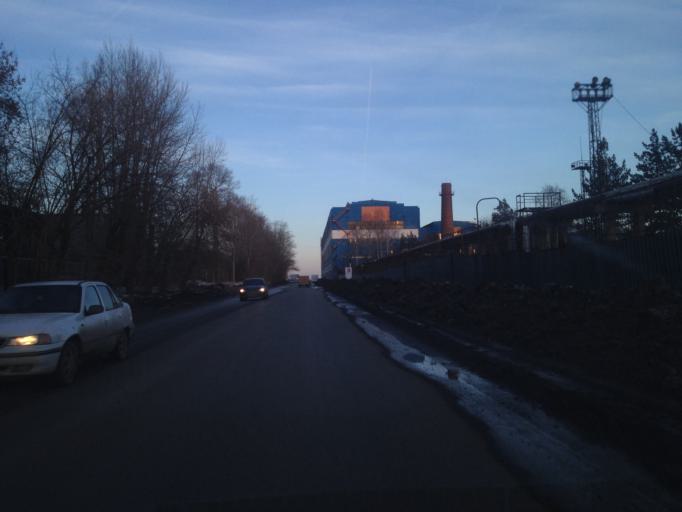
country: RU
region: Sverdlovsk
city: Istok
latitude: 56.7587
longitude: 60.7202
